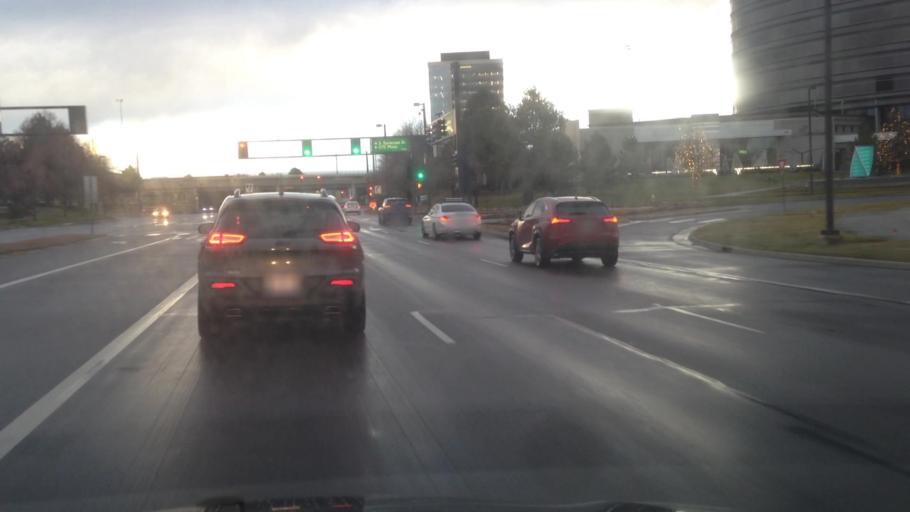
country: US
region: Colorado
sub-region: Arapahoe County
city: Castlewood
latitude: 39.6240
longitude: -104.8986
